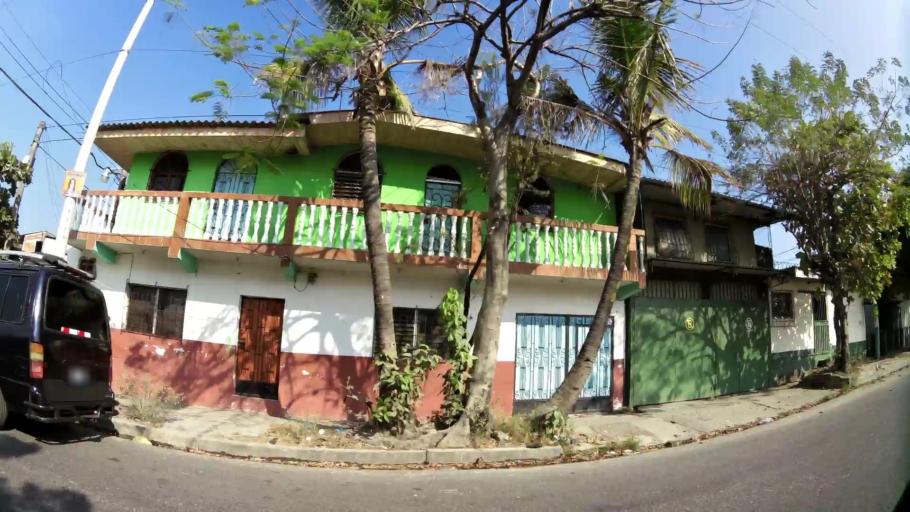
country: SV
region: San Salvador
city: Ilopango
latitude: 13.7188
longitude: -89.1059
